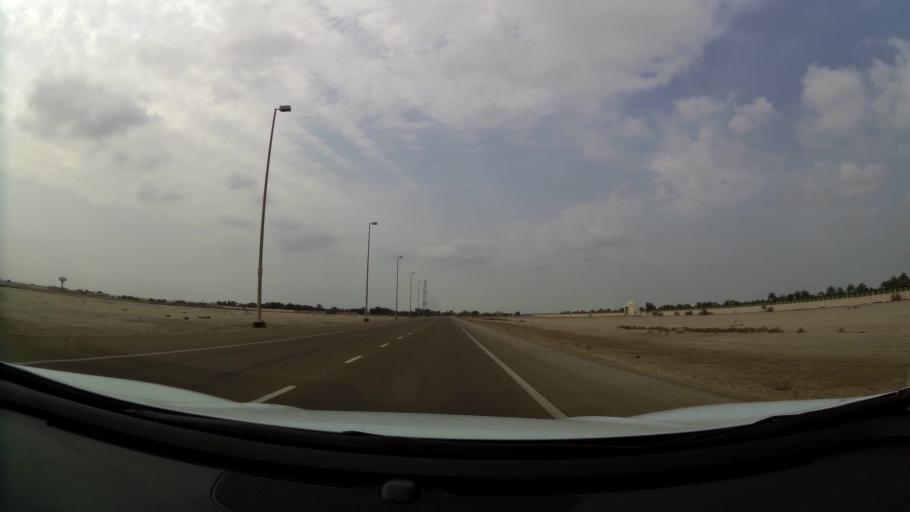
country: AE
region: Abu Dhabi
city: Abu Dhabi
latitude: 24.6267
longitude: 54.6495
